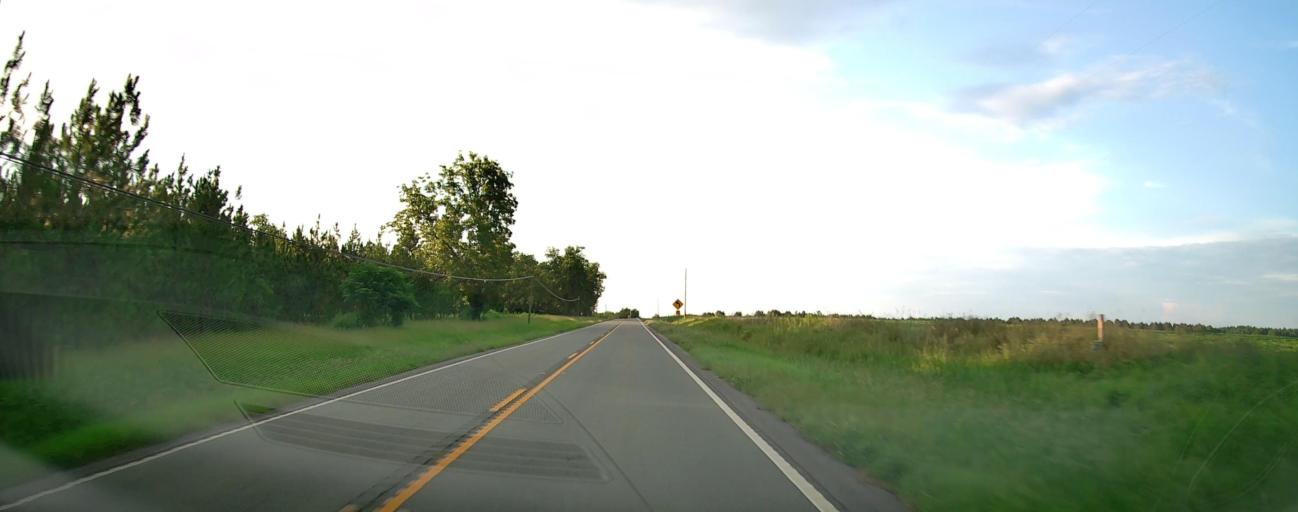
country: US
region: Georgia
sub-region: Taylor County
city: Reynolds
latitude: 32.5843
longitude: -84.0896
